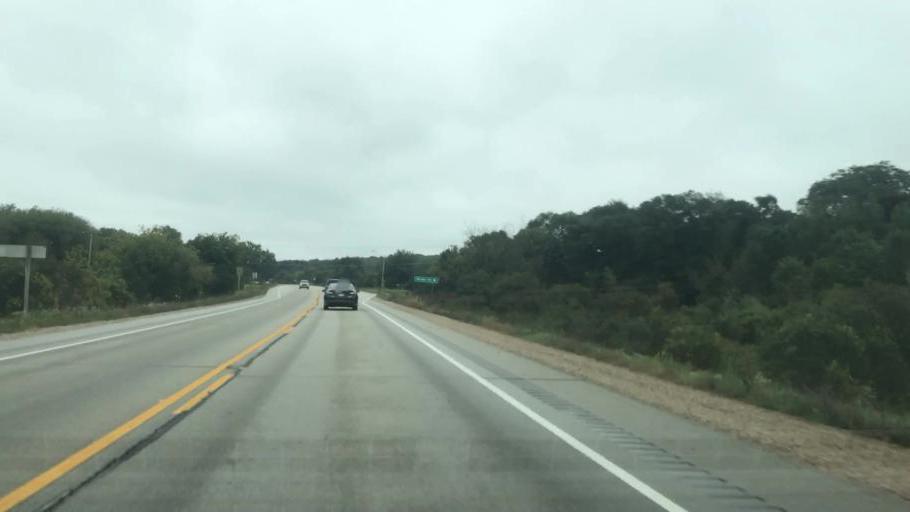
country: US
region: Wisconsin
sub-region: Waukesha County
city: Wales
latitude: 42.9633
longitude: -88.3238
